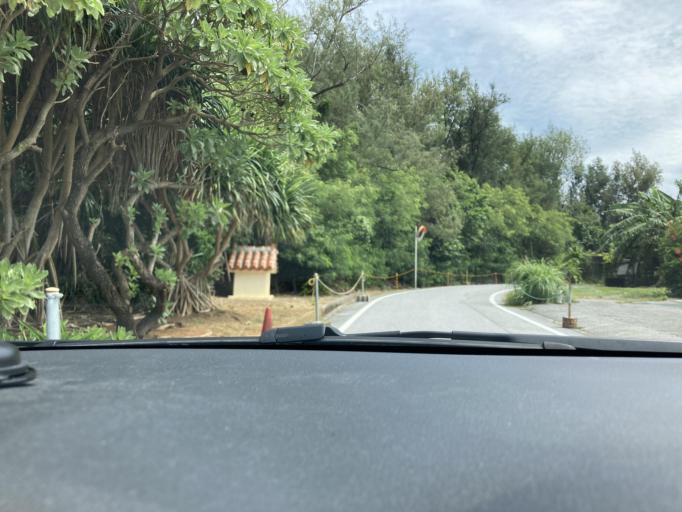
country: JP
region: Okinawa
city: Ishikawa
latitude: 26.4424
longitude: 127.7725
